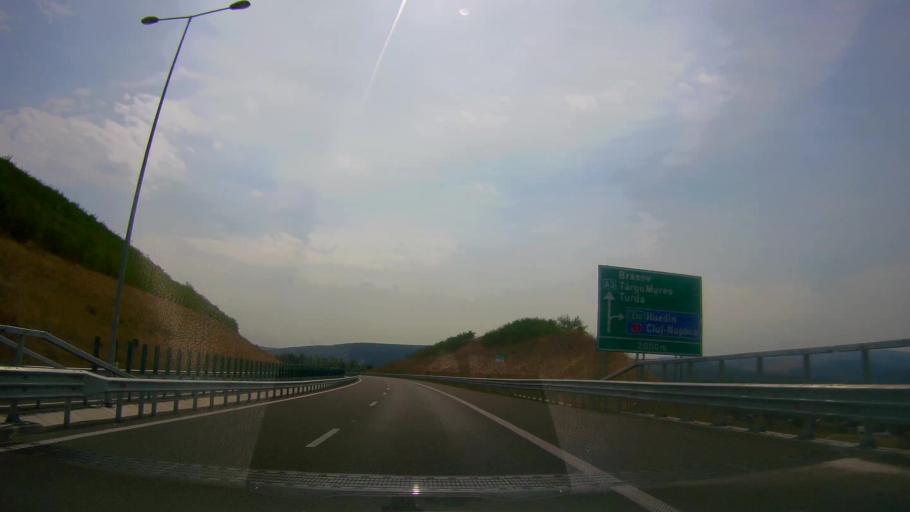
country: RO
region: Cluj
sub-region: Comuna Gilau
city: Gilau
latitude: 46.7668
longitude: 23.3839
